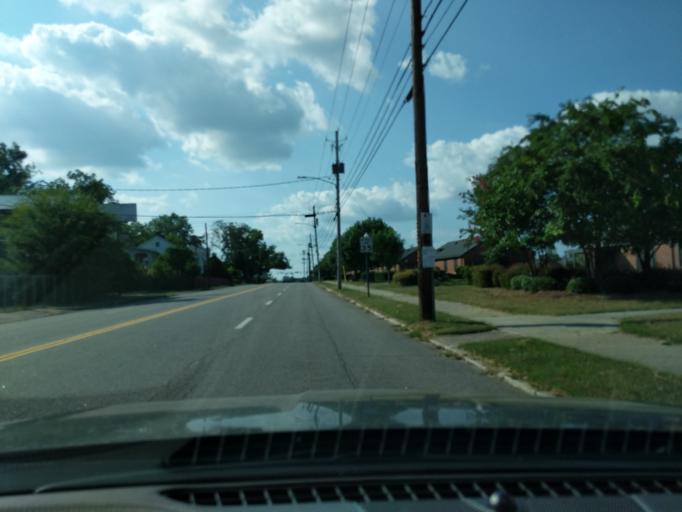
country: US
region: Georgia
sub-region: Richmond County
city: Augusta
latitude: 33.4879
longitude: -82.0032
